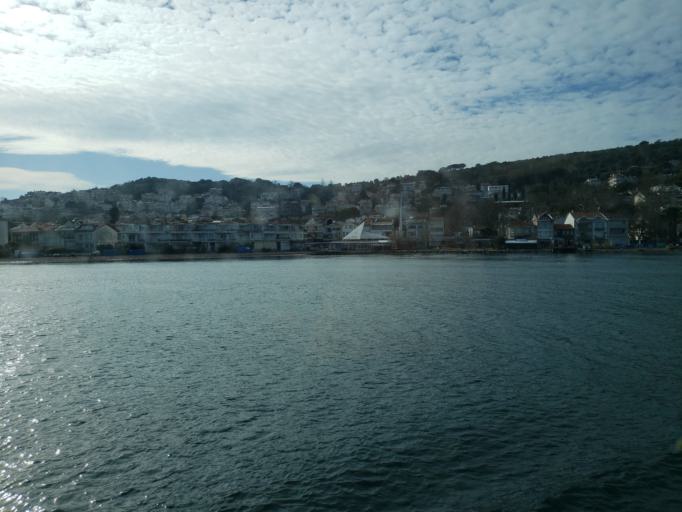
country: TR
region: Istanbul
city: Kinali
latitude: 40.9092
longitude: 29.0576
